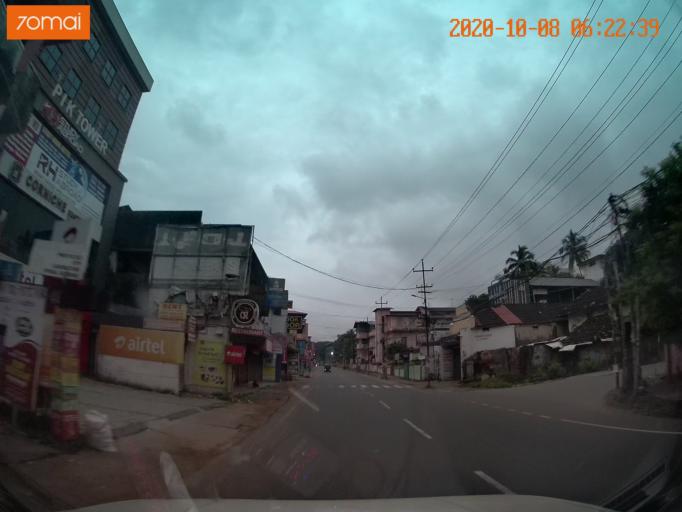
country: IN
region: Kerala
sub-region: Thrissur District
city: Trichur
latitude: 10.5231
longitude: 76.2218
